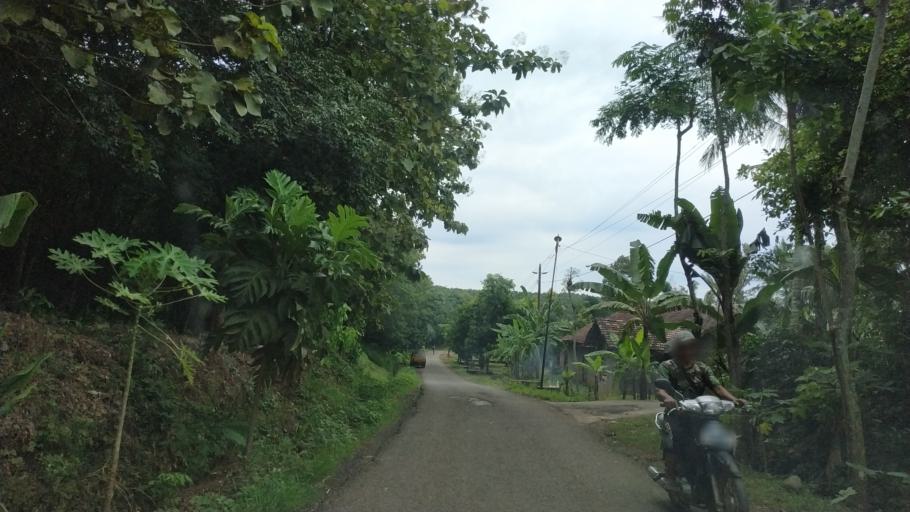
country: ID
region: Central Java
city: Krajan Tegalombo
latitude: -6.4405
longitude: 110.9820
